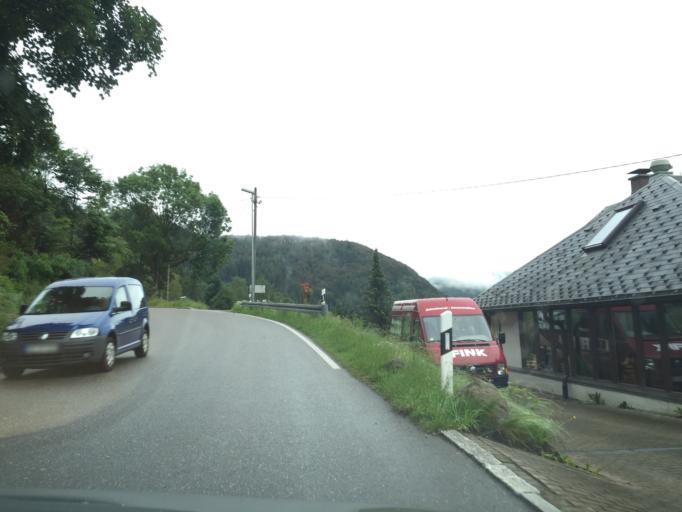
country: DE
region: Baden-Wuerttemberg
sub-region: Freiburg Region
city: Todtnau
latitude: 47.8430
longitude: 7.9286
